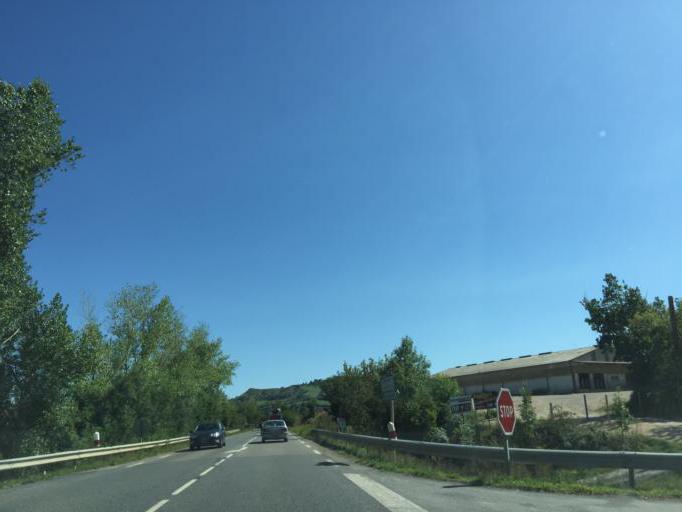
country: FR
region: Midi-Pyrenees
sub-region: Departement de l'Aveyron
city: Severac-le-Chateau
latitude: 44.3377
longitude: 3.0278
